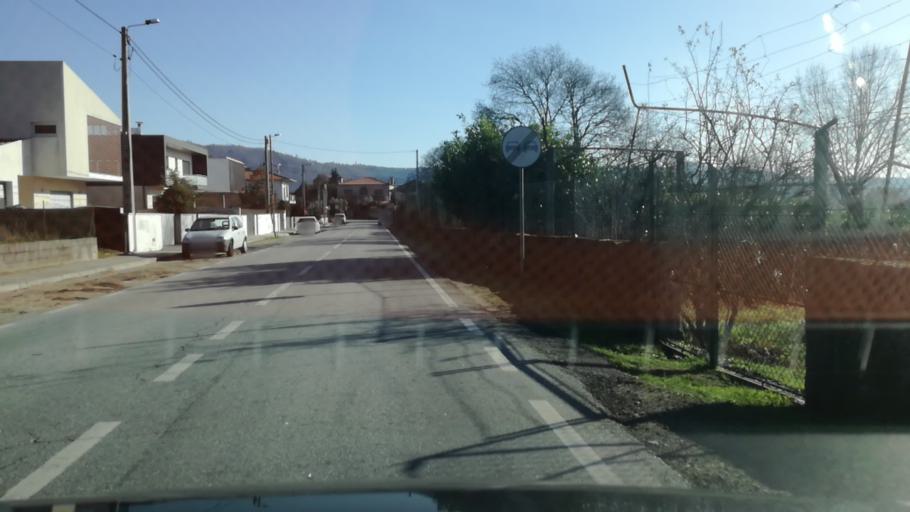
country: PT
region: Braga
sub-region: Guimaraes
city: Ponte
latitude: 41.5159
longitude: -8.3136
